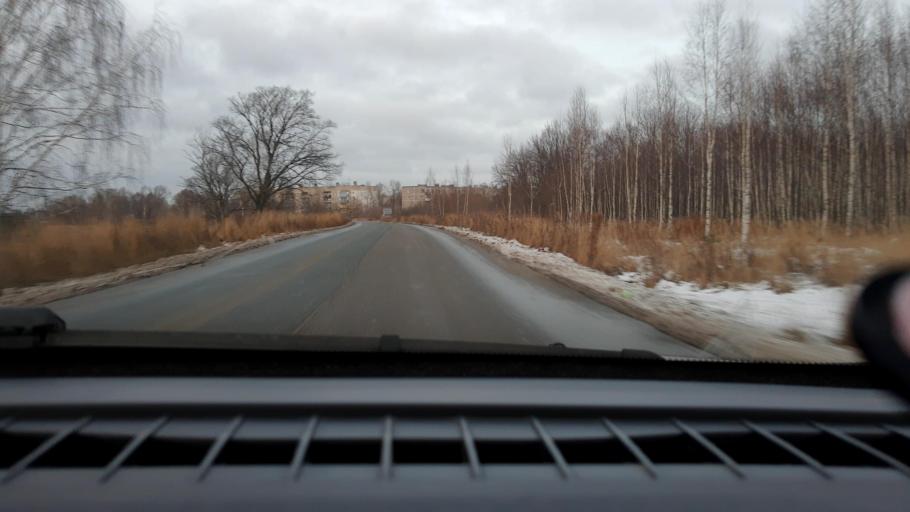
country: RU
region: Nizjnij Novgorod
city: Gorbatovka
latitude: 56.2412
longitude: 43.7437
